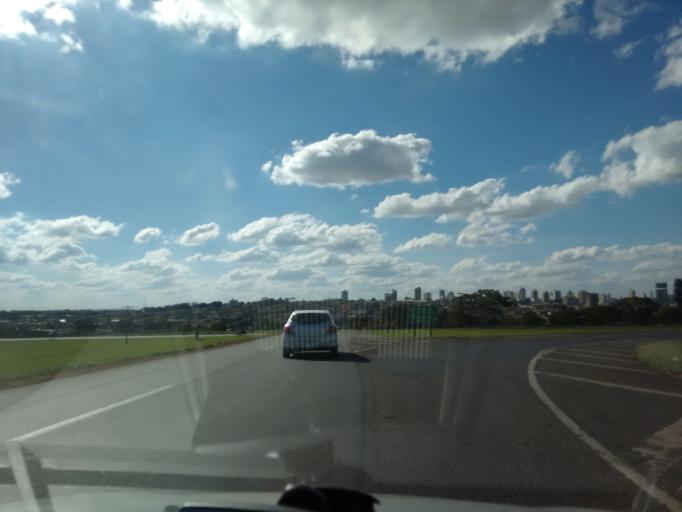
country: BR
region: Sao Paulo
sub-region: Araraquara
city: Araraquara
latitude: -21.8182
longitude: -48.1774
